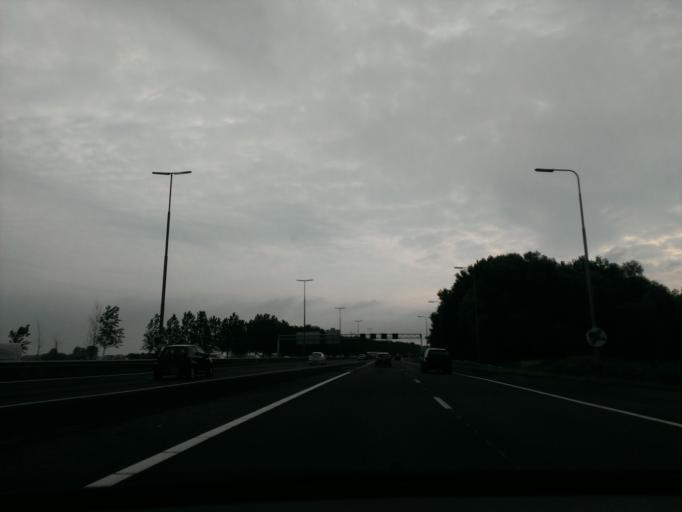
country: NL
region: Gelderland
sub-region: Gemeente Hattem
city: Hattem
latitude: 52.4911
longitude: 6.0333
